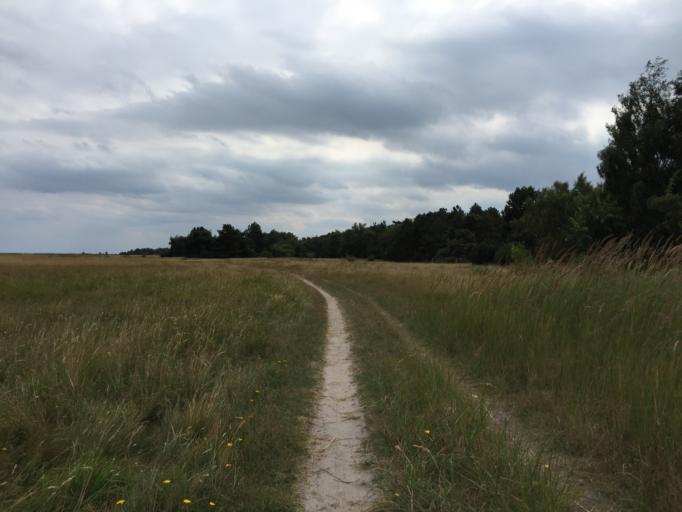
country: DE
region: Mecklenburg-Vorpommern
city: Hiddensee
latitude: 54.5050
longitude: 13.0734
